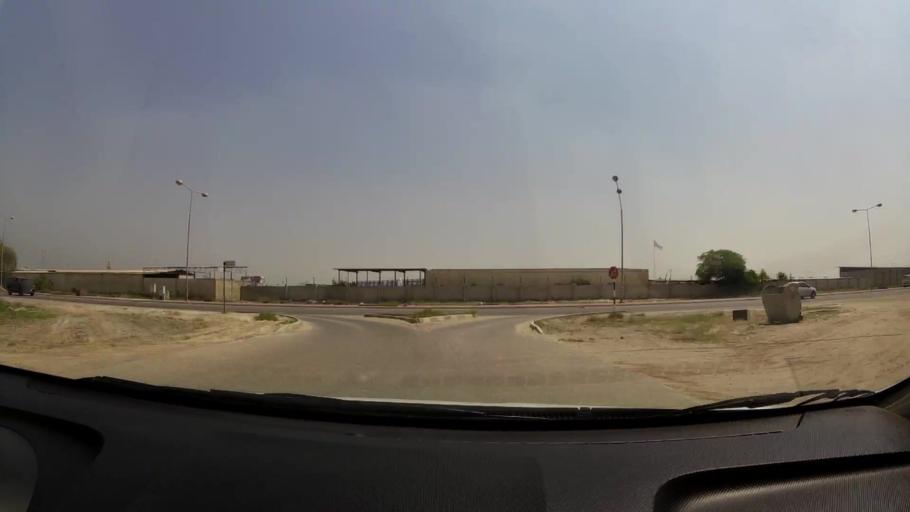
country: AE
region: Umm al Qaywayn
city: Umm al Qaywayn
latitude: 25.5633
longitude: 55.5579
